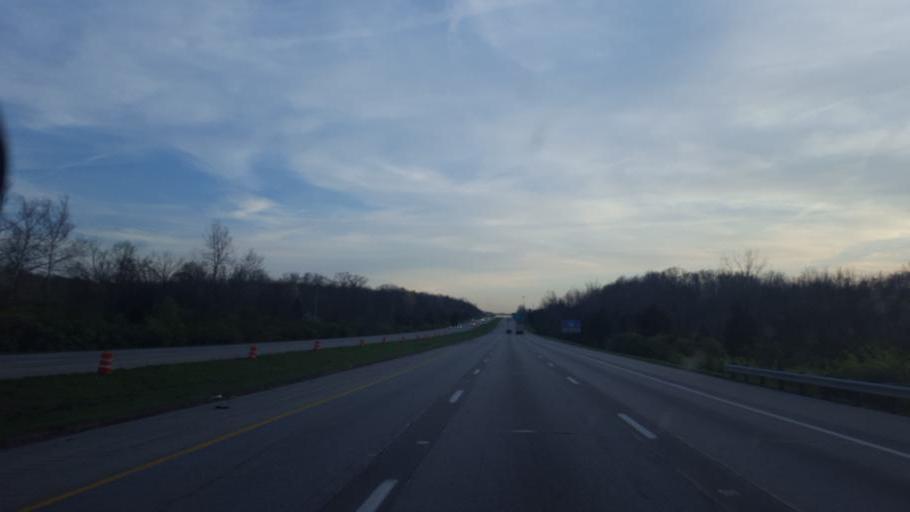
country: US
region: Ohio
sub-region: Warren County
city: Kings Mills
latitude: 39.3701
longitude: -84.2509
